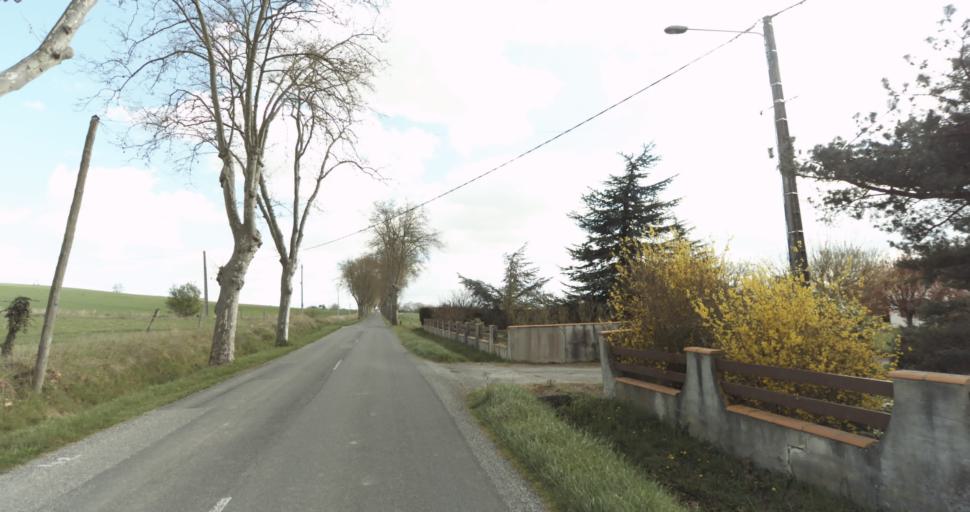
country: FR
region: Midi-Pyrenees
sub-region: Departement de la Haute-Garonne
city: Auterive
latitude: 43.3709
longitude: 1.4696
